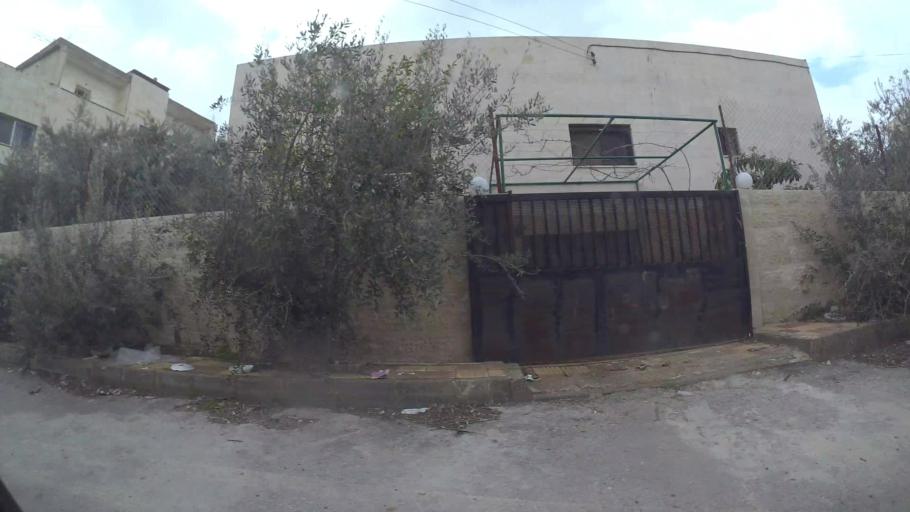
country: JO
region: Amman
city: Al Jubayhah
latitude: 32.0387
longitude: 35.8273
